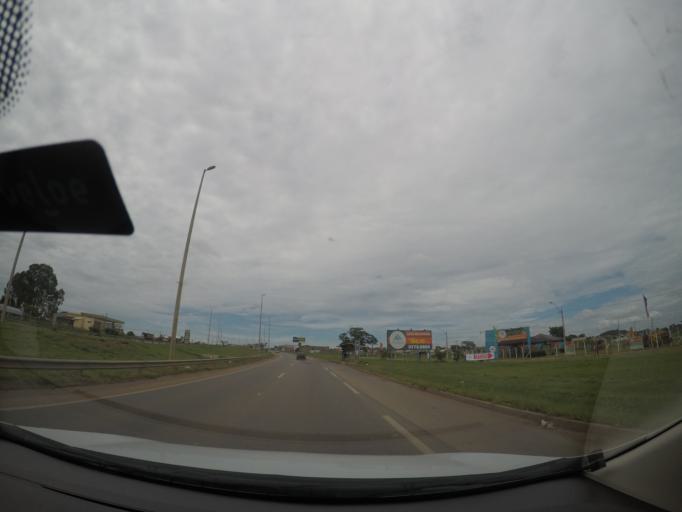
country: BR
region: Goias
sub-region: Goianira
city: Goianira
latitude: -16.5508
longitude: -49.4065
